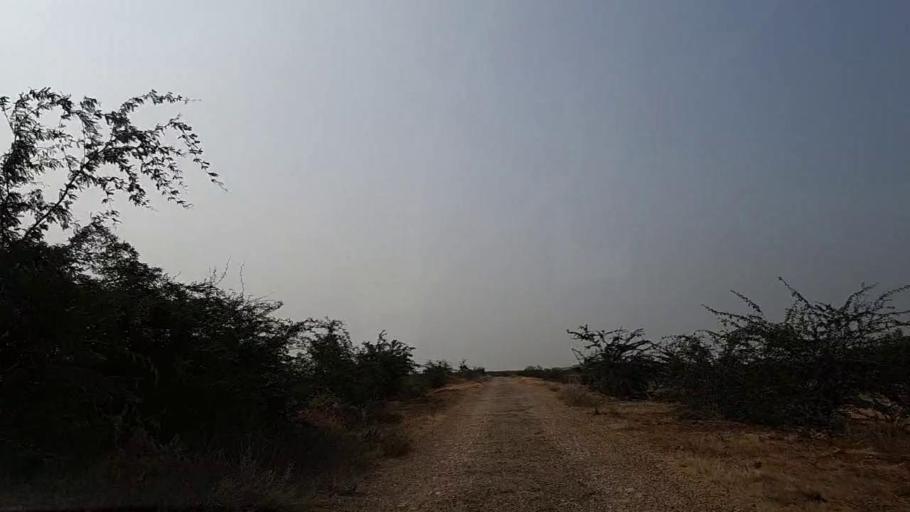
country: PK
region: Sindh
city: Thatta
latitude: 24.7238
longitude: 67.8328
